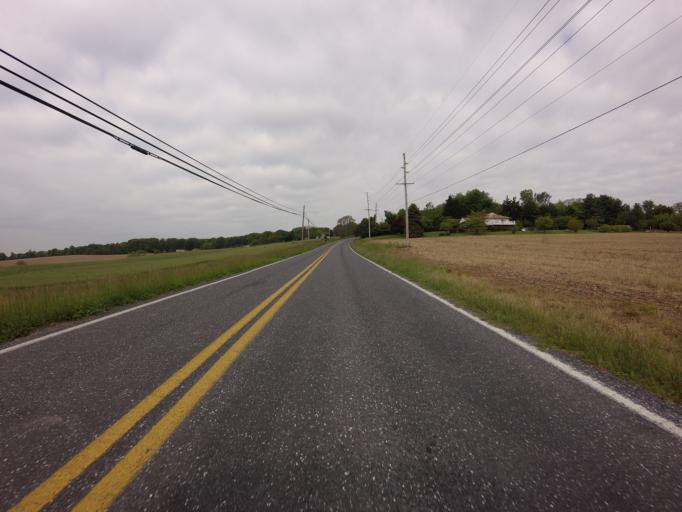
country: US
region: Maryland
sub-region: Frederick County
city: Green Valley
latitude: 39.2864
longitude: -77.2757
